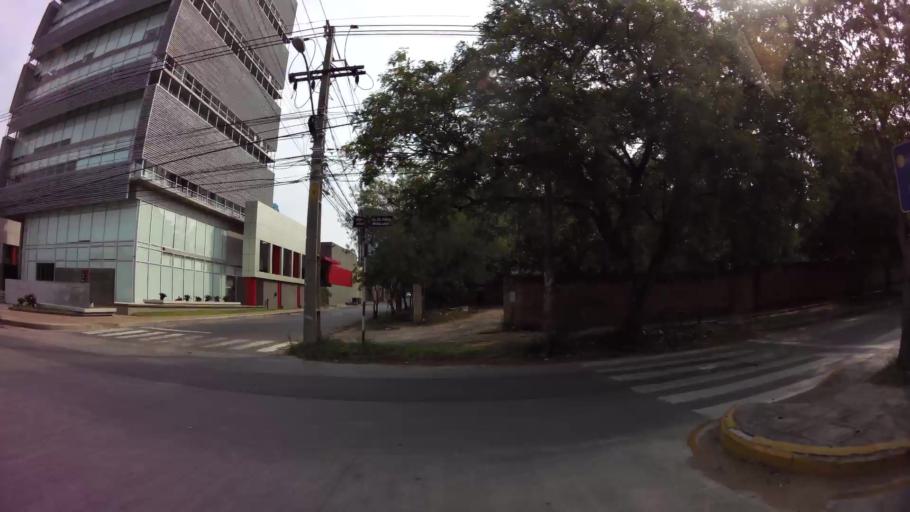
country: PY
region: Central
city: Fernando de la Mora
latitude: -25.2800
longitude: -57.5607
